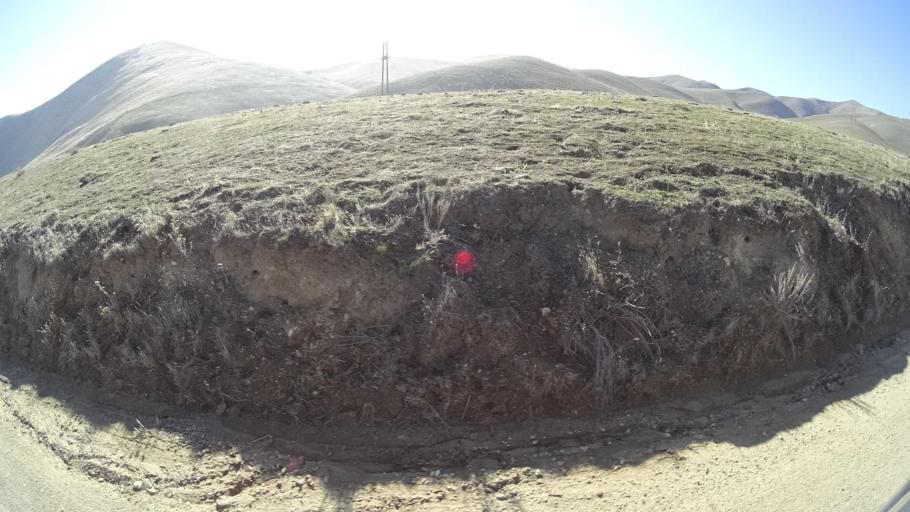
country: US
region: California
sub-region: Kern County
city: Taft Heights
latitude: 35.2290
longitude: -119.6723
